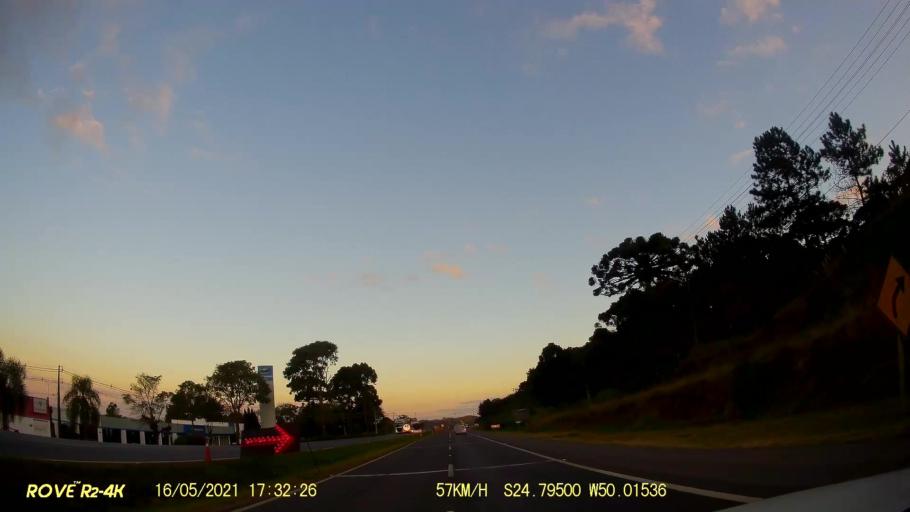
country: BR
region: Parana
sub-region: Castro
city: Castro
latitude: -24.7952
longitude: -50.0154
